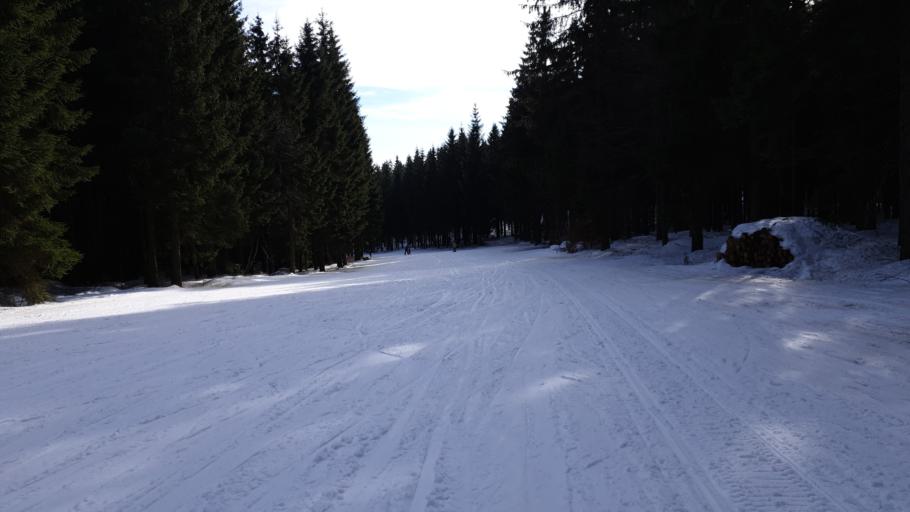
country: DE
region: Bavaria
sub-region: Upper Franconia
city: Bischofsgrun
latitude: 50.0218
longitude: 11.8107
